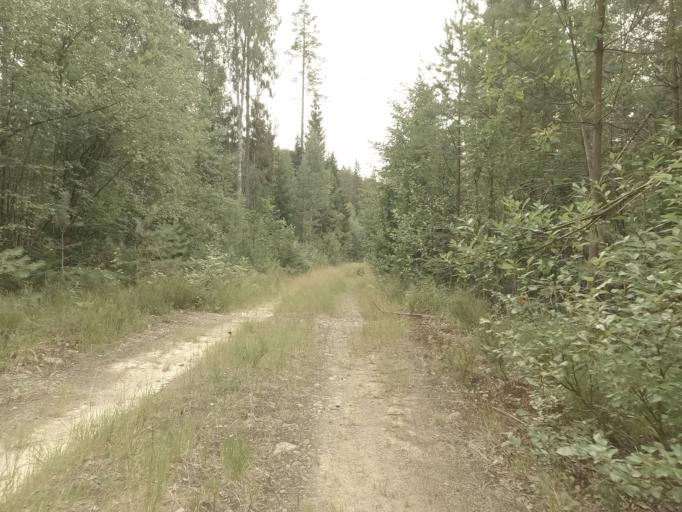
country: RU
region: Leningrad
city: Kamennogorsk
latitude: 61.0193
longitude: 29.1623
